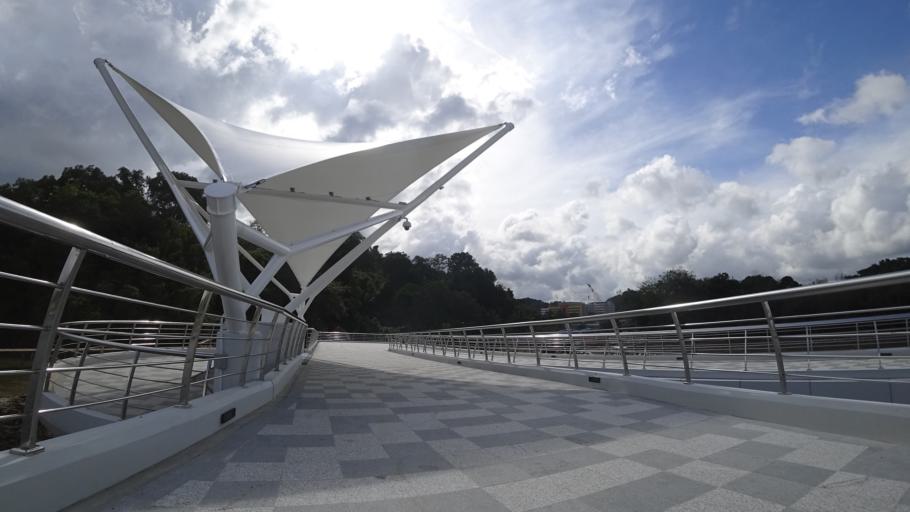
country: BN
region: Brunei and Muara
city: Bandar Seri Begawan
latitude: 4.8879
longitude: 114.9364
